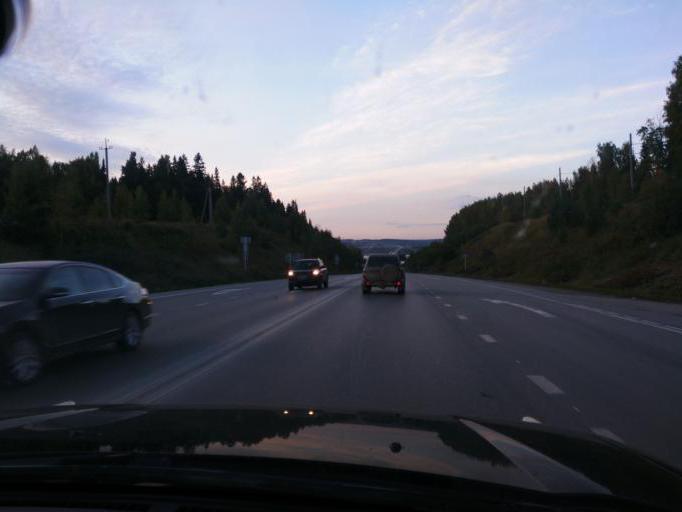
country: RU
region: Perm
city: Polazna
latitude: 58.1500
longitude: 56.4188
